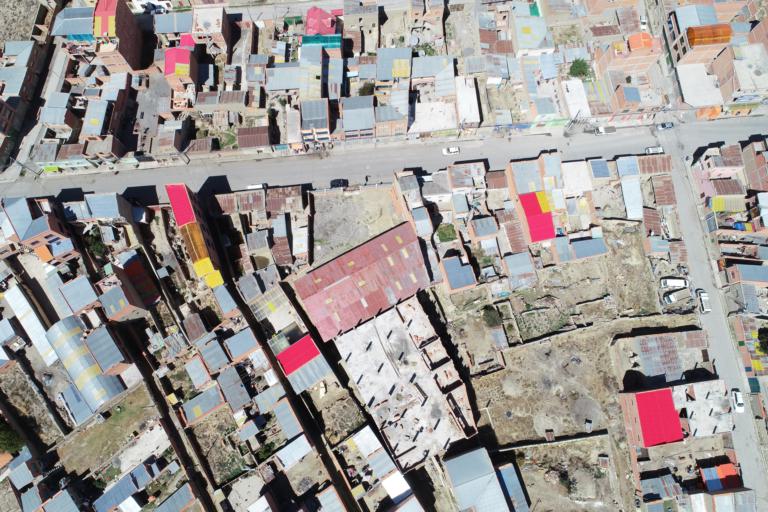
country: BO
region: La Paz
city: Achacachi
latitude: -16.0466
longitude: -68.6821
